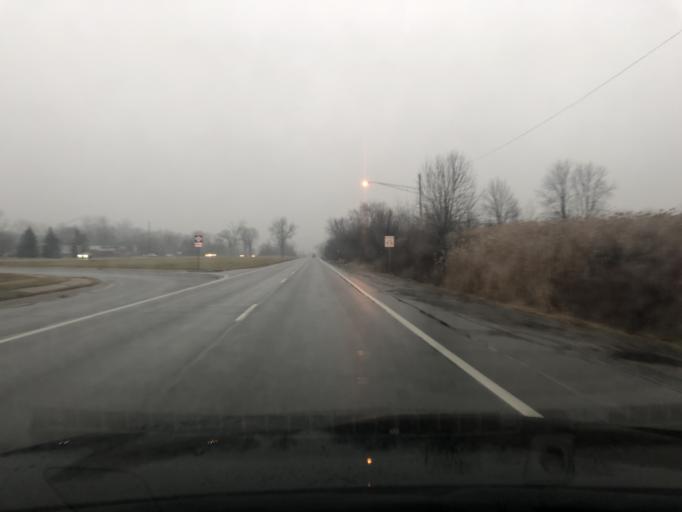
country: US
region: Michigan
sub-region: Wayne County
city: Gibraltar
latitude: 42.1111
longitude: -83.2160
